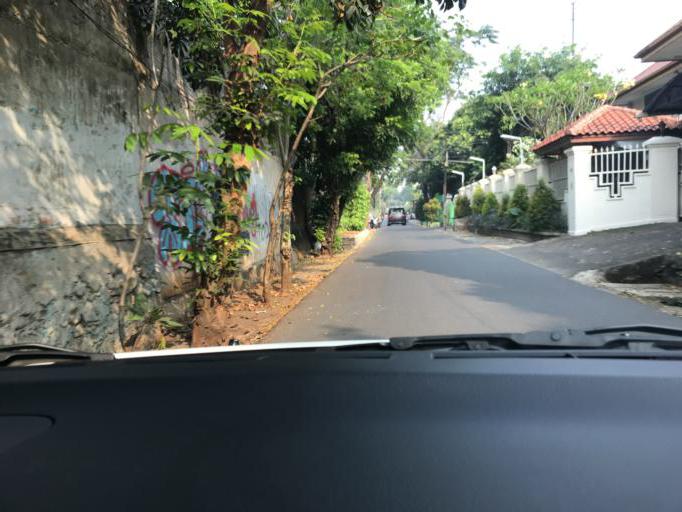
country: ID
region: Jakarta Raya
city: Jakarta
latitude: -6.2704
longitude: 106.8058
